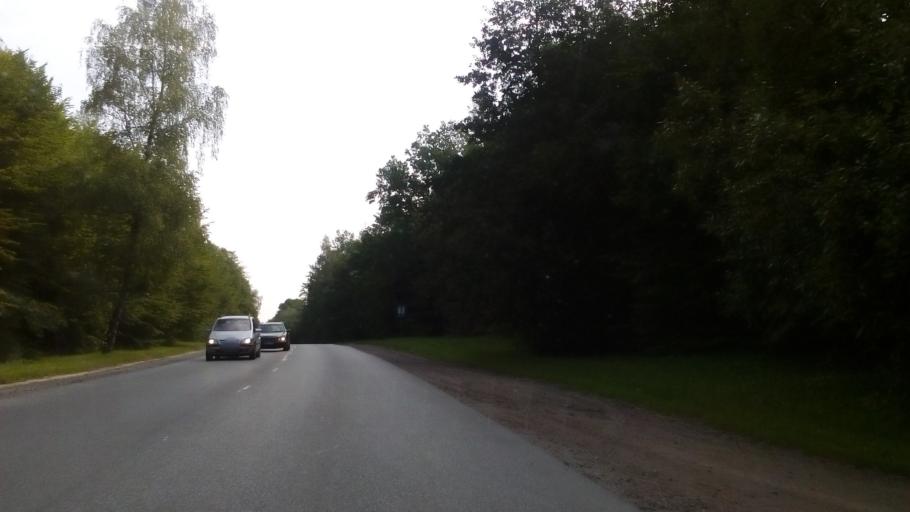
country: LT
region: Alytaus apskritis
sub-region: Alytus
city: Alytus
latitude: 54.3867
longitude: 24.0081
